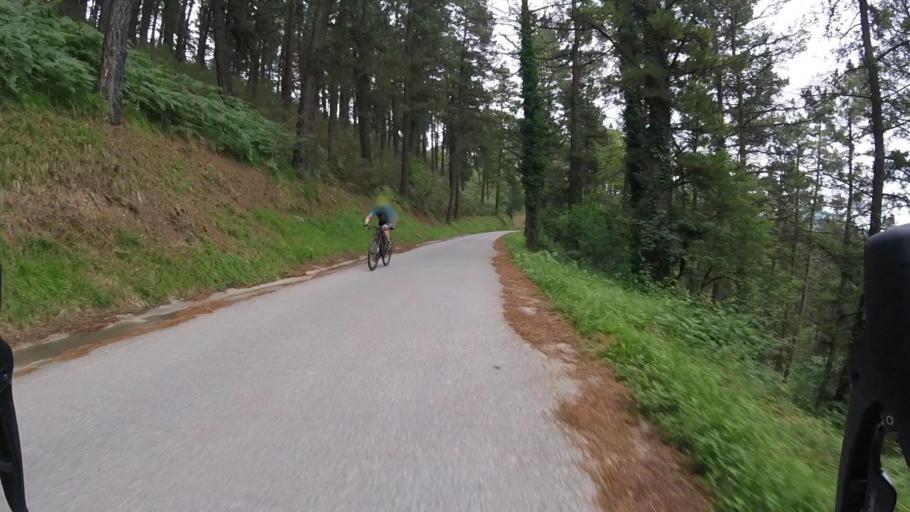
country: ES
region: Basque Country
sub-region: Provincia de Guipuzcoa
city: Errenteria
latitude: 43.2609
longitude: -1.8919
